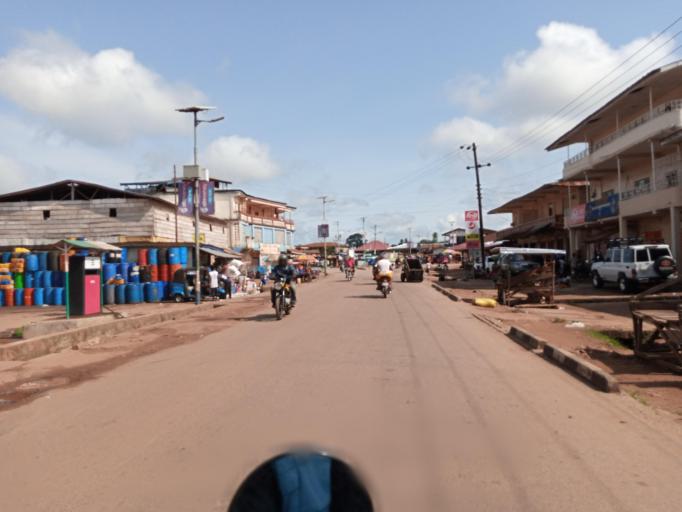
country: SL
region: Southern Province
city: Bo
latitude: 7.9652
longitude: -11.7359
